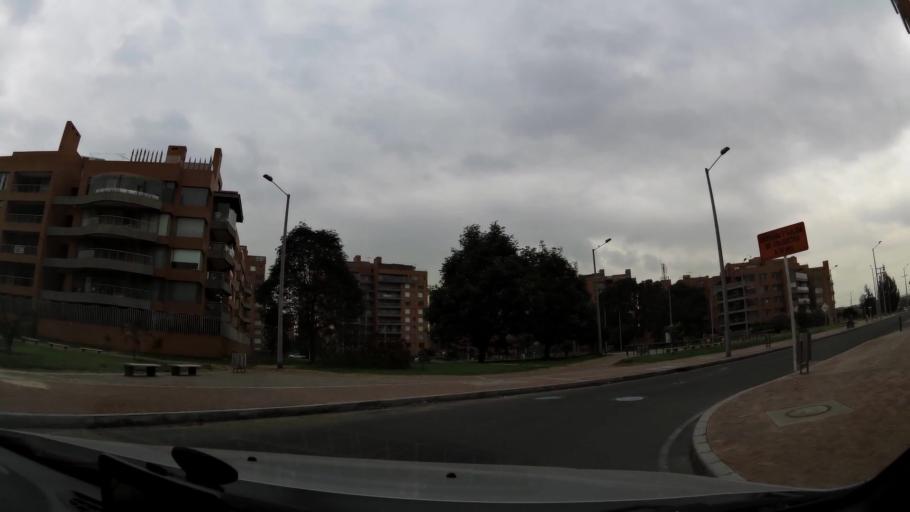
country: CO
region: Bogota D.C.
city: Bogota
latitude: 4.6613
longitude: -74.1131
